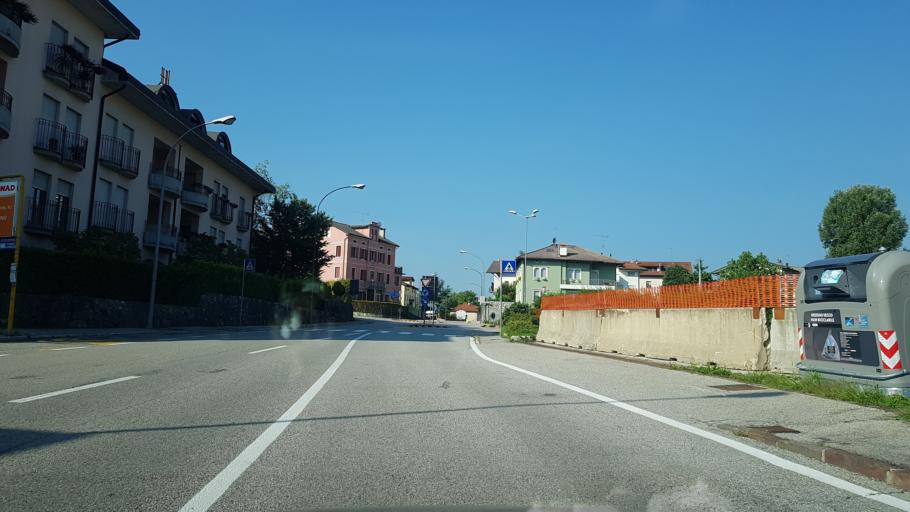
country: IT
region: Veneto
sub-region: Provincia di Belluno
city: Belluno
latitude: 46.1337
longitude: 12.2179
